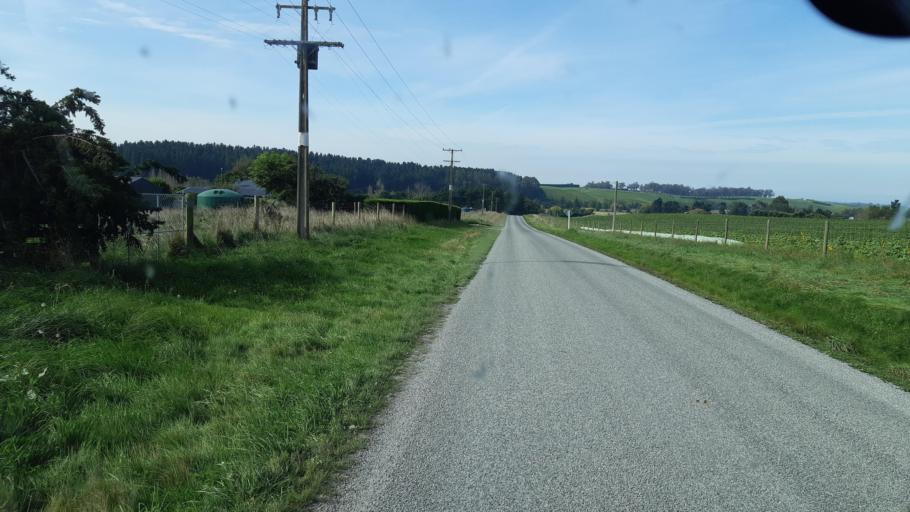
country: NZ
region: Canterbury
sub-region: Timaru District
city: Pleasant Point
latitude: -44.3318
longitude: 171.1581
